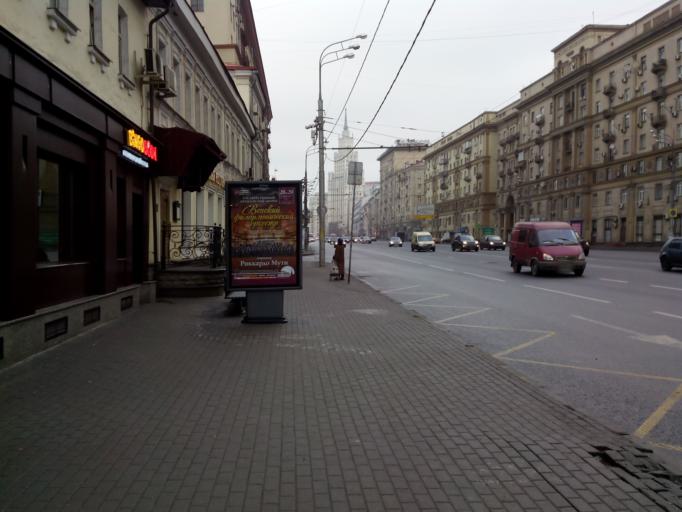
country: RU
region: Moscow
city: Taganskiy
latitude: 55.7645
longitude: 37.6553
